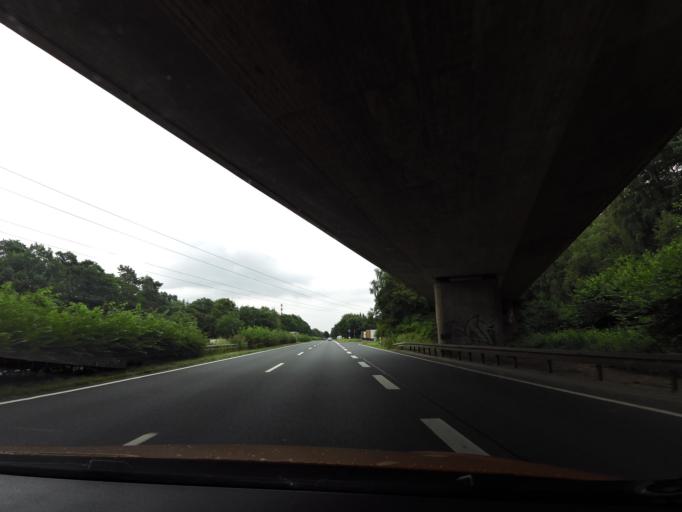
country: DE
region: Lower Saxony
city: Neustadt am Rubenberge
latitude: 52.4852
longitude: 9.4941
